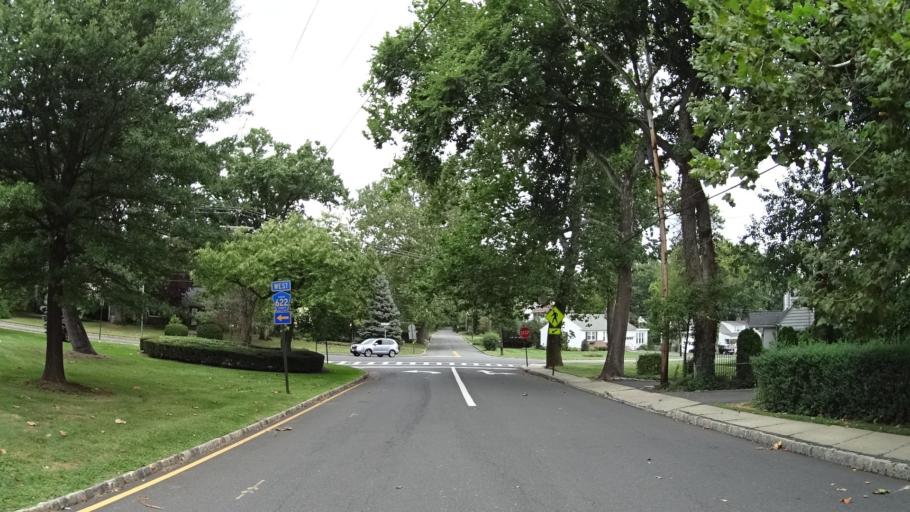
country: US
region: New Jersey
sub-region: Union County
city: New Providence
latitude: 40.7034
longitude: -74.3712
